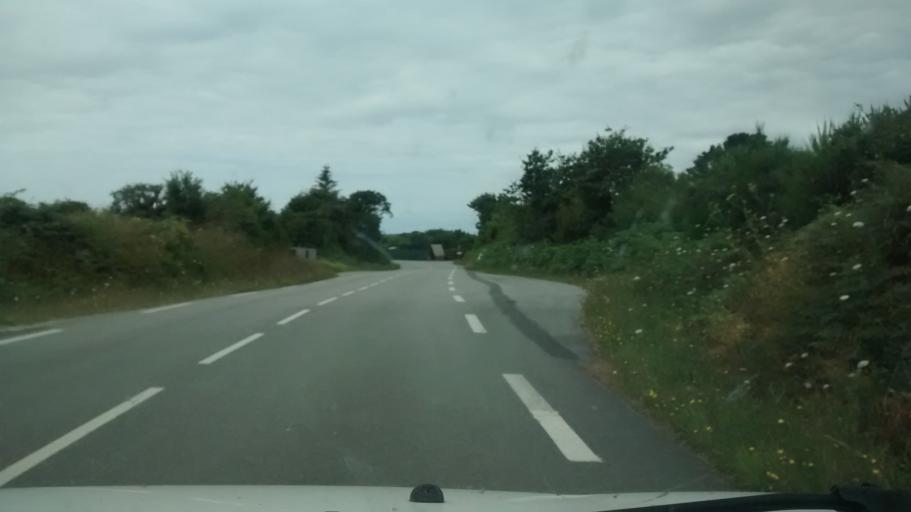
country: FR
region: Brittany
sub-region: Departement du Finistere
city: Lanveoc
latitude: 48.3348
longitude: -4.4330
